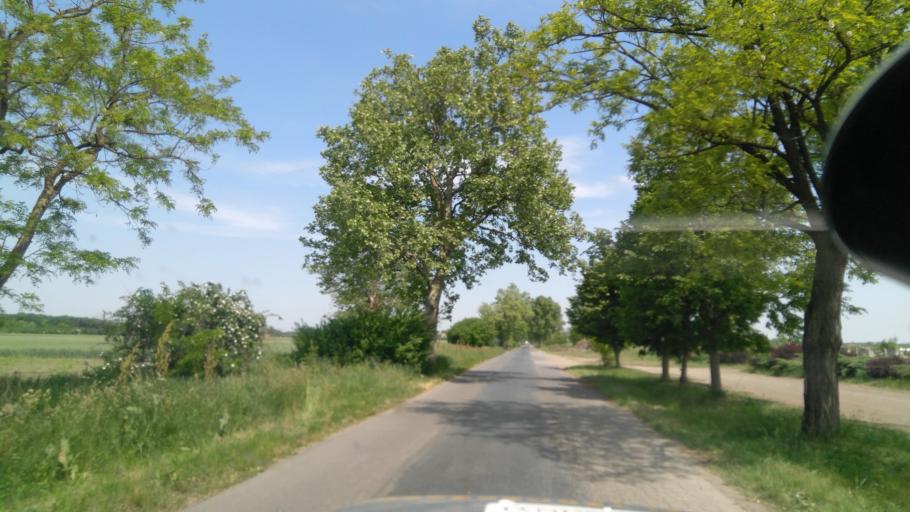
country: HU
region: Csongrad
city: Szekkutas
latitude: 46.5762
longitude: 20.4654
